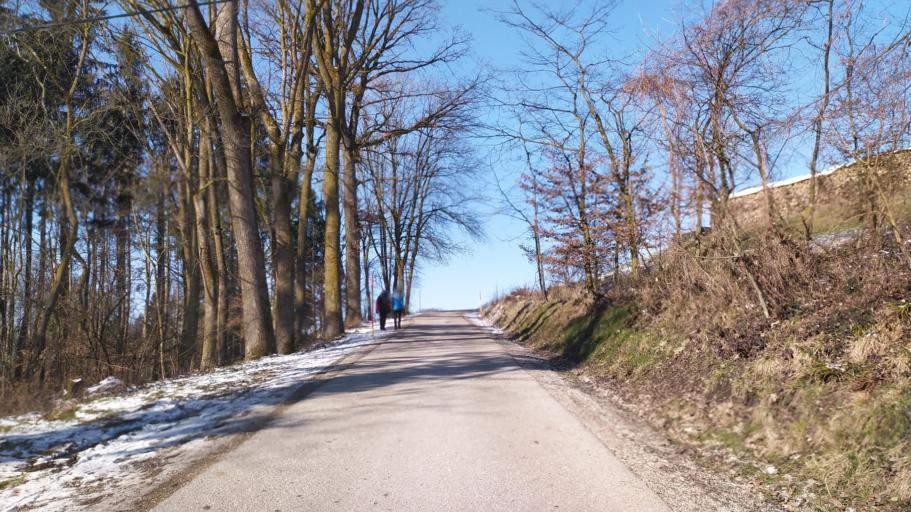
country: AT
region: Upper Austria
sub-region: Politischer Bezirk Urfahr-Umgebung
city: Ottensheim
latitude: 48.3182
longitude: 14.2171
